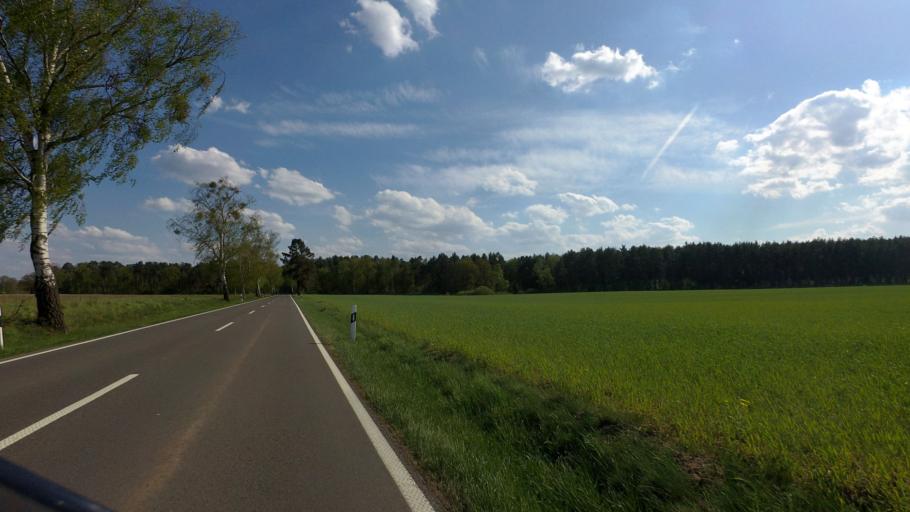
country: DE
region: Brandenburg
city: Templin
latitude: 53.0609
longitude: 13.5207
